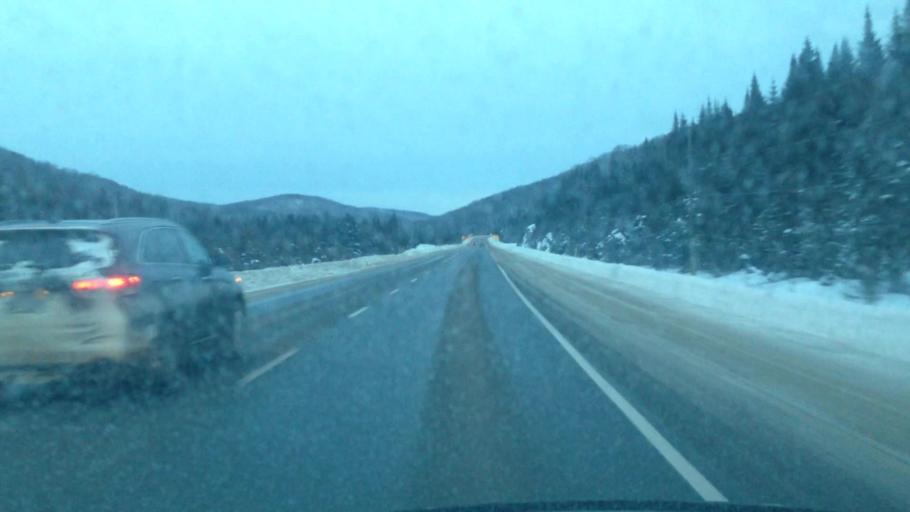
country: CA
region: Quebec
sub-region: Laurentides
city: Mont-Tremblant
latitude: 46.1237
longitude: -74.4475
